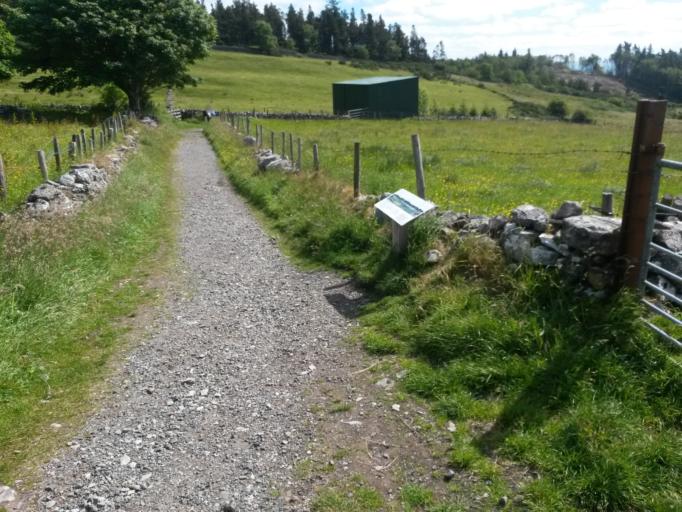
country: IE
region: Connaught
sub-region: Sligo
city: Strandhill
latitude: 54.2569
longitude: -8.5652
